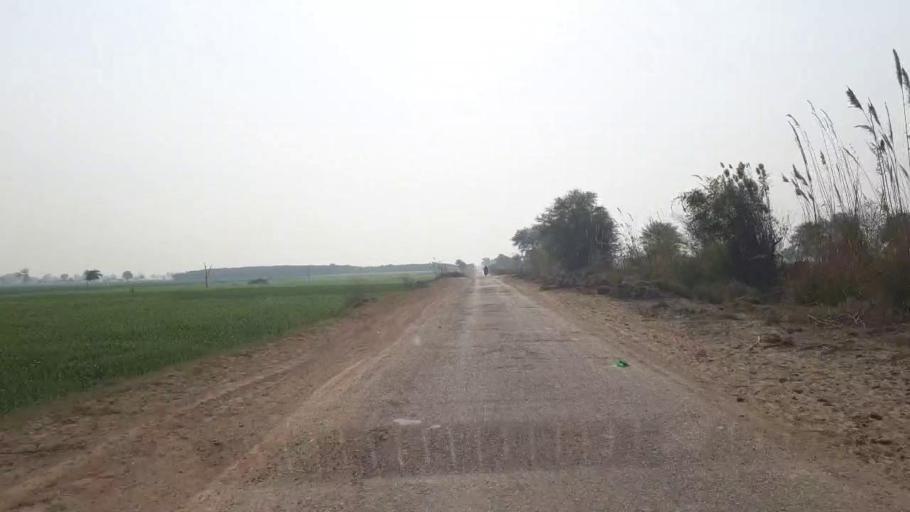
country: PK
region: Sindh
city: Hala
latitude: 25.9202
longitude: 68.4460
